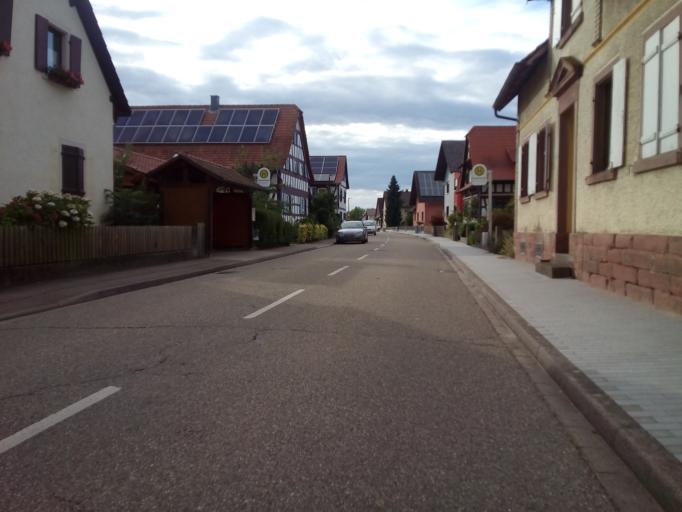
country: DE
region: Baden-Wuerttemberg
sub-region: Karlsruhe Region
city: Lichtenau
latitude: 48.6943
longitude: 7.9875
